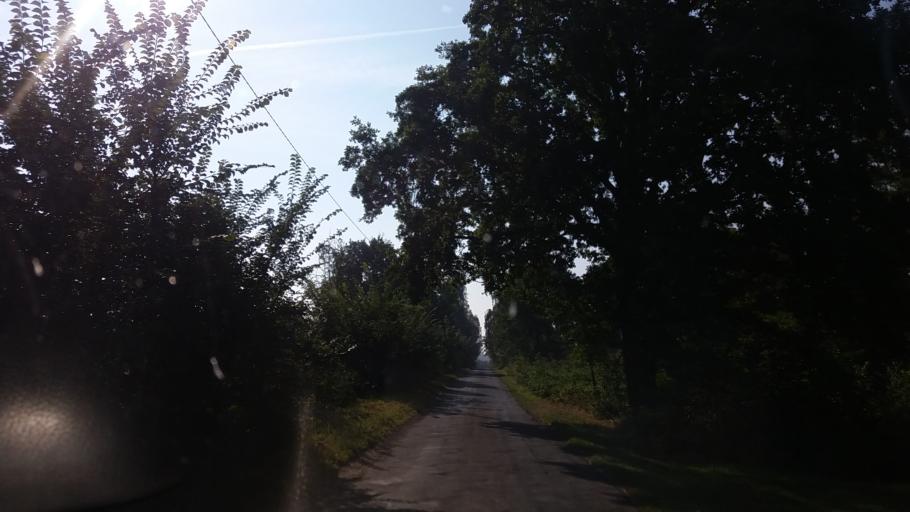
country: PL
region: West Pomeranian Voivodeship
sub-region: Powiat choszczenski
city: Pelczyce
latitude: 53.0122
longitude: 15.3404
